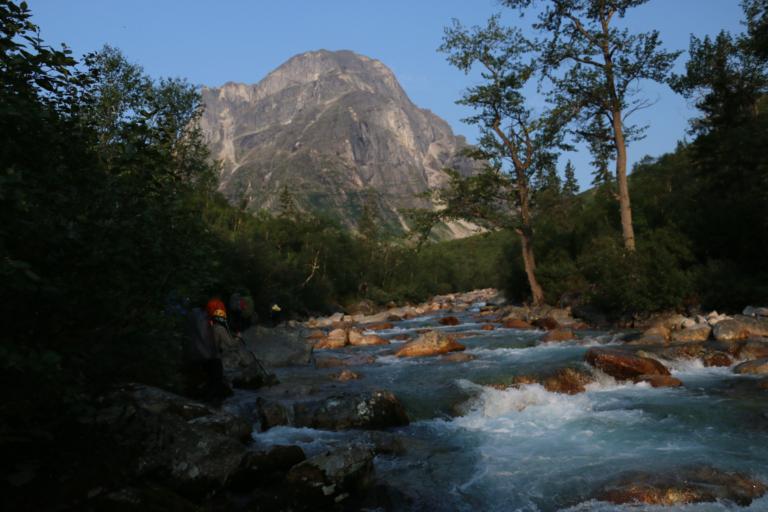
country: RU
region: Respublika Buryatiya
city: Novyy Uoyan
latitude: 56.2726
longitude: 111.1081
